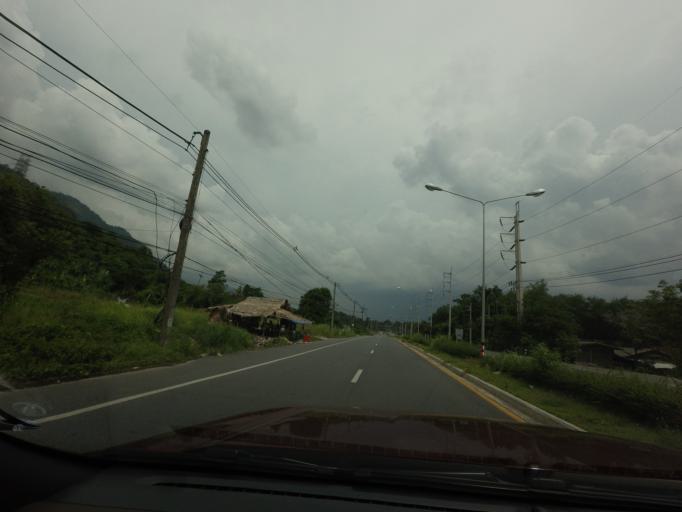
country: TH
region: Yala
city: Yala
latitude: 6.4789
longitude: 101.2656
